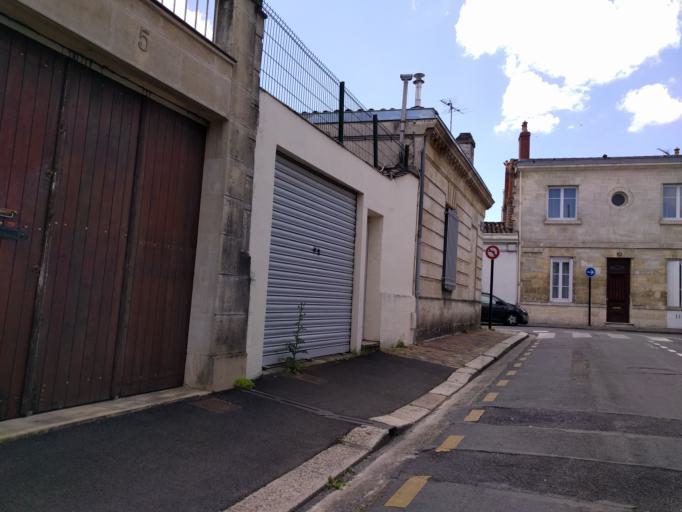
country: FR
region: Aquitaine
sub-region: Departement de la Gironde
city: Bordeaux
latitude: 44.8219
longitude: -0.5783
